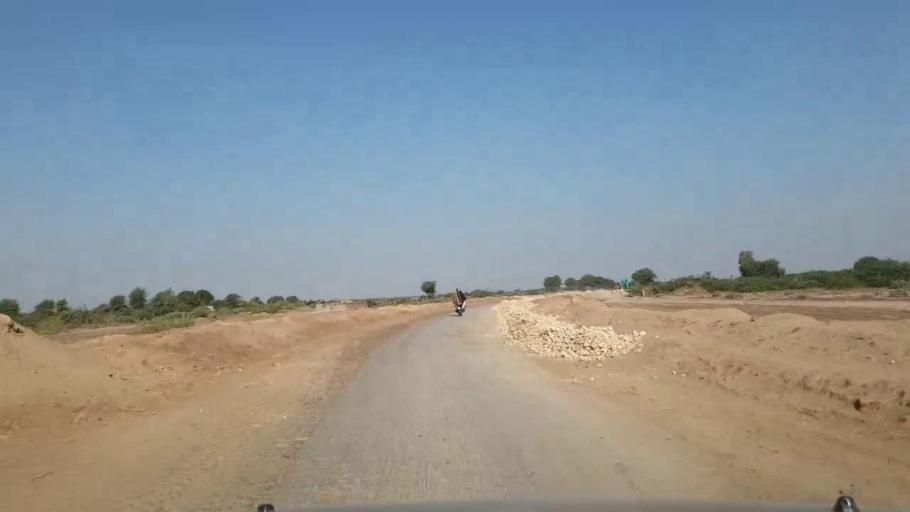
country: PK
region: Sindh
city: Digri
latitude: 24.9659
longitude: 69.1124
